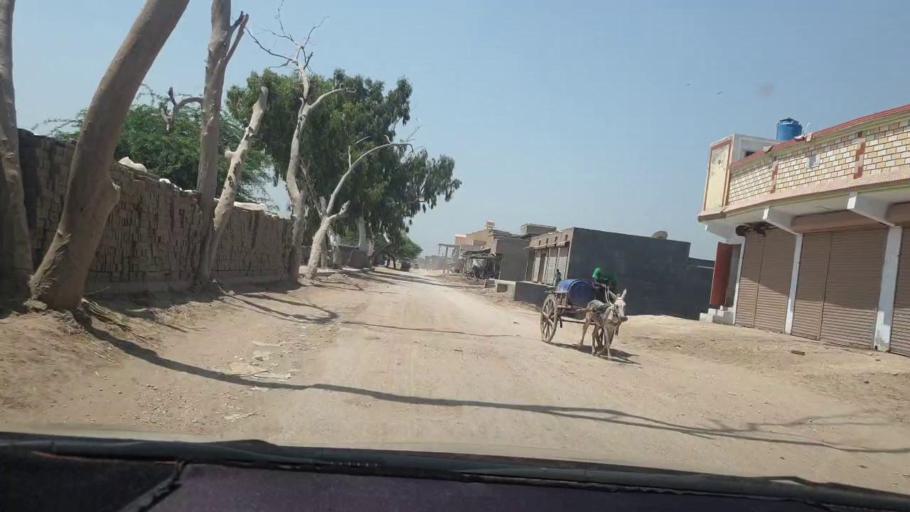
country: PK
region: Sindh
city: Kambar
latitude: 27.5923
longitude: 68.0118
